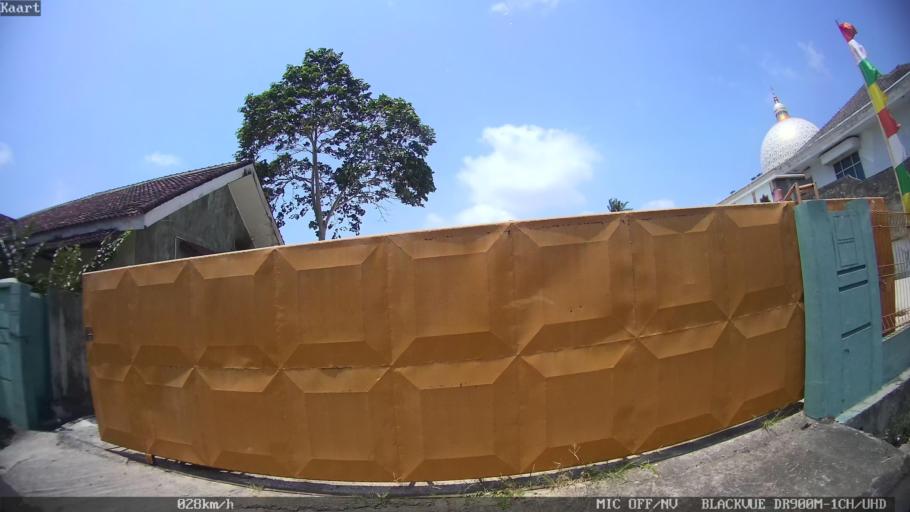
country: ID
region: Lampung
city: Kedaton
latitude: -5.3742
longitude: 105.2700
